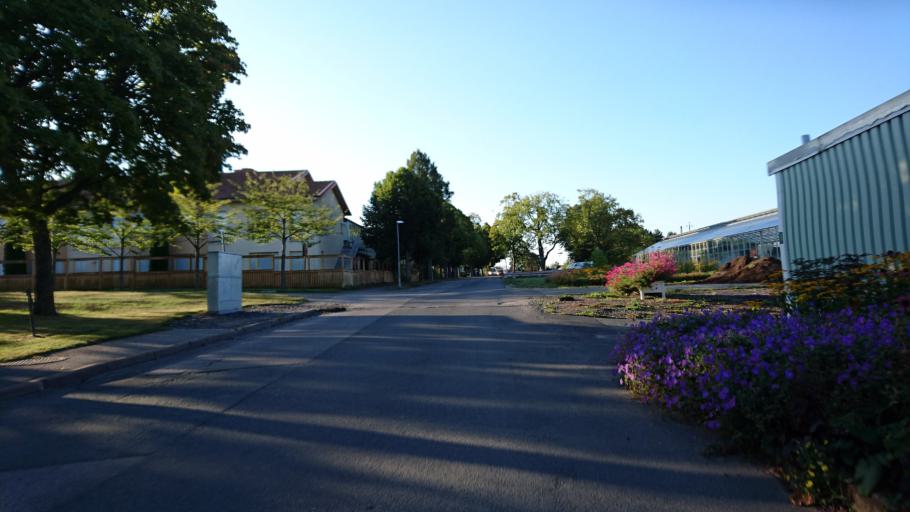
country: SE
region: Joenkoeping
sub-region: Jonkopings Kommun
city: Jonkoping
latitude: 57.8142
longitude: 14.1518
